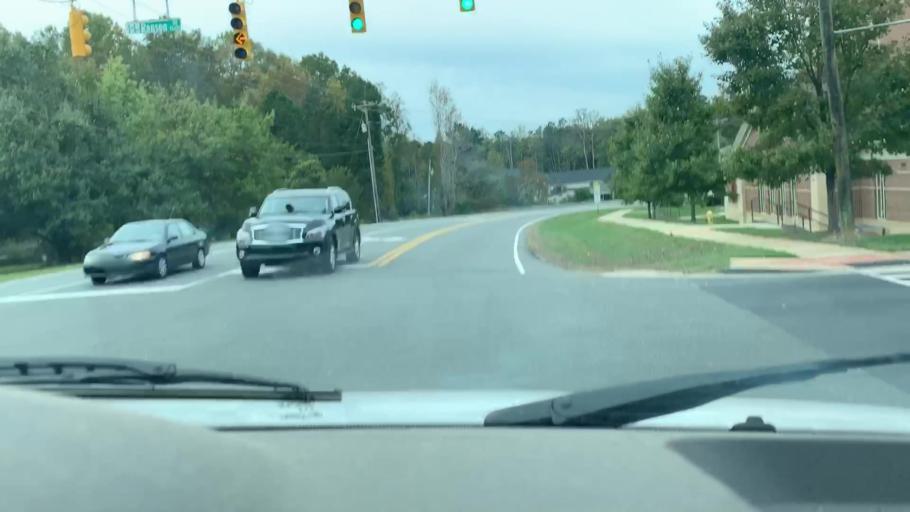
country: US
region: North Carolina
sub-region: Mecklenburg County
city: Huntersville
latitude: 35.4208
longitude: -80.8653
